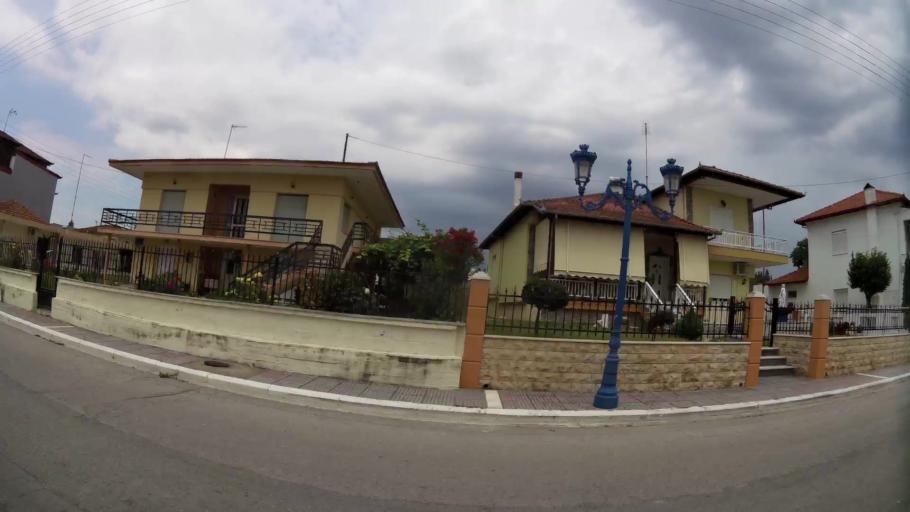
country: GR
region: Central Macedonia
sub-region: Nomos Pierias
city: Kallithea
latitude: 40.2760
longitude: 22.5801
